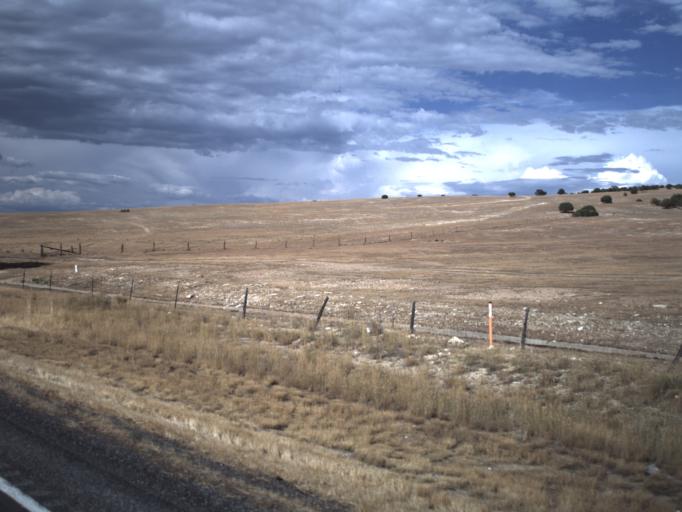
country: US
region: Utah
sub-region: Sanpete County
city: Ephraim
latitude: 39.4127
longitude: -111.5608
